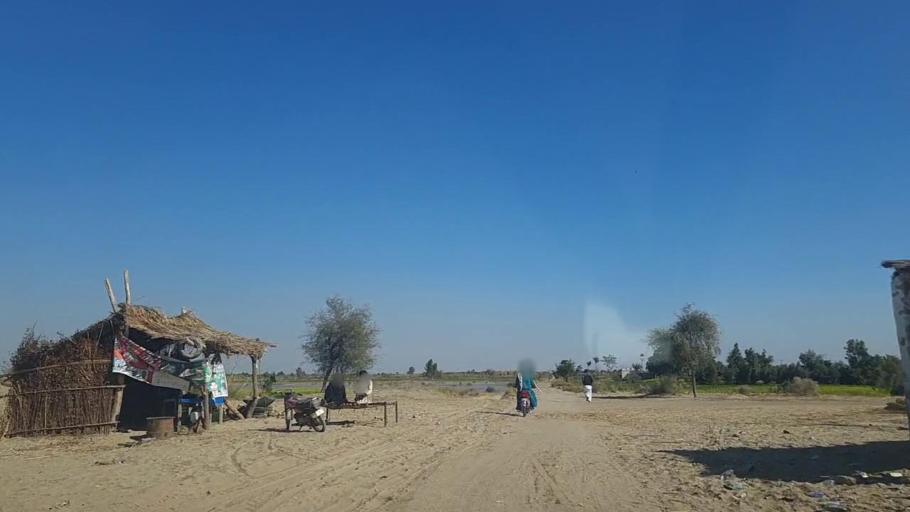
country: PK
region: Sindh
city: Sanghar
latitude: 26.2092
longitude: 68.8921
